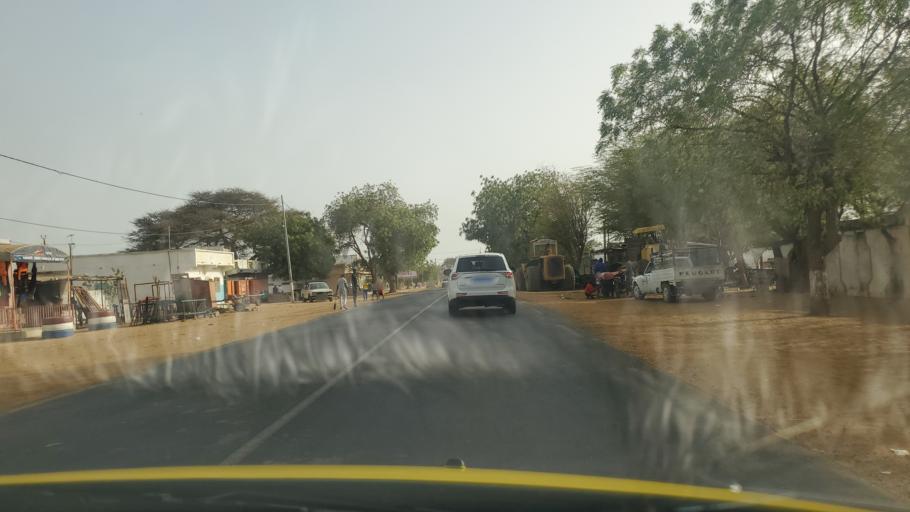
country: SN
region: Thies
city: Mekhe
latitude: 15.2836
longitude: -16.5268
